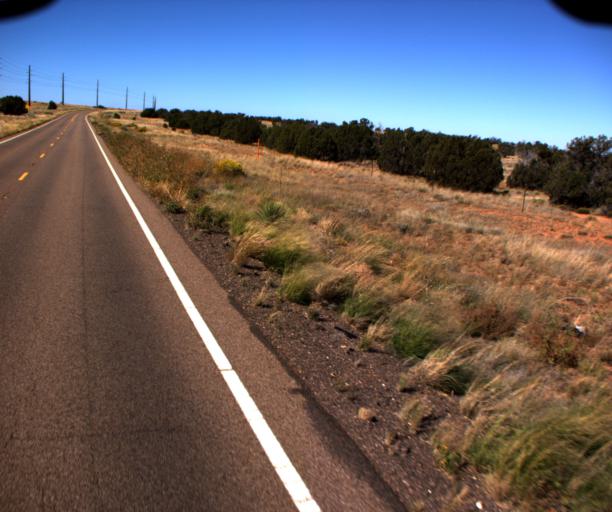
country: US
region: Arizona
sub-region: Navajo County
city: Taylor
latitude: 34.4822
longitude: -110.2988
